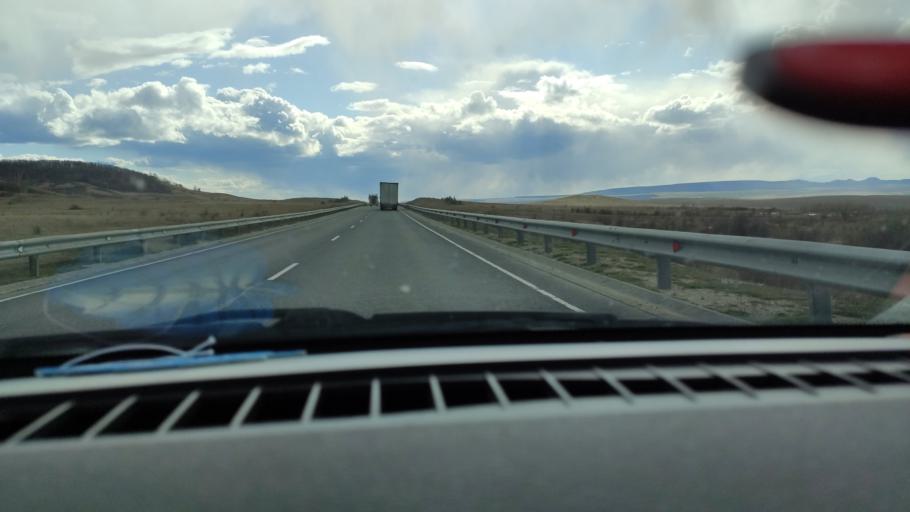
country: RU
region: Saratov
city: Alekseyevka
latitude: 52.3617
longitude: 47.9550
